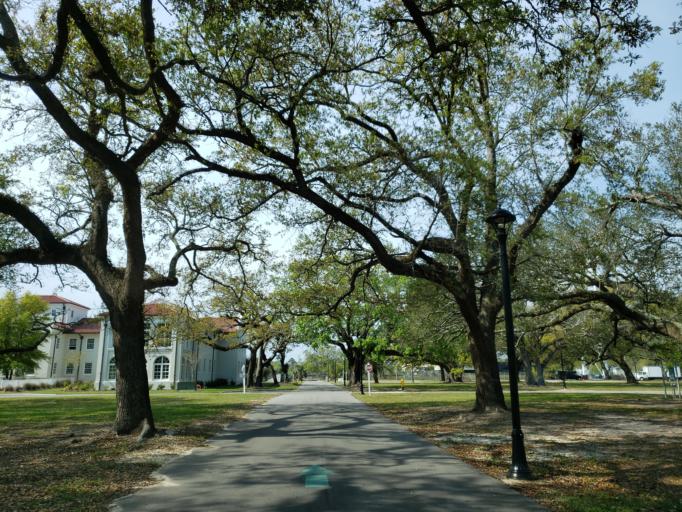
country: US
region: Mississippi
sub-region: Harrison County
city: Gulfport
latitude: 30.3786
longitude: -89.0507
